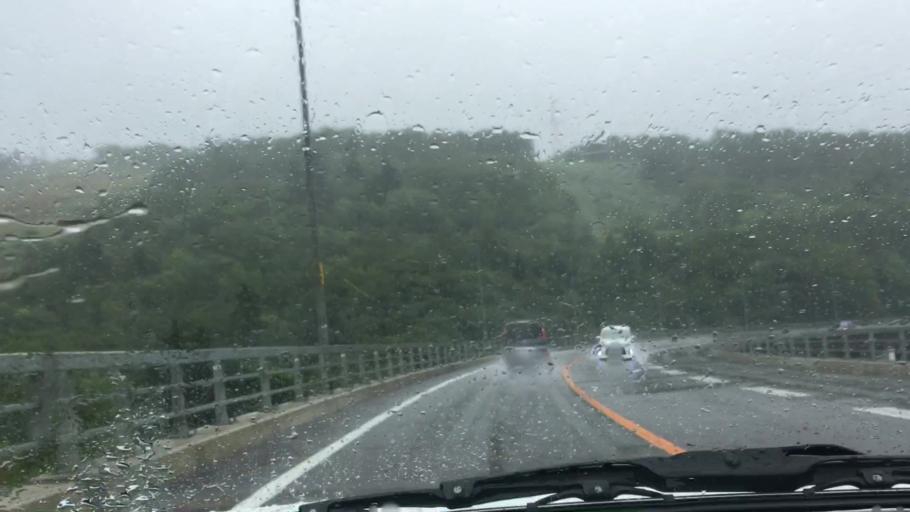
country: JP
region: Hokkaido
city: Sapporo
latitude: 42.8519
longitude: 141.0918
